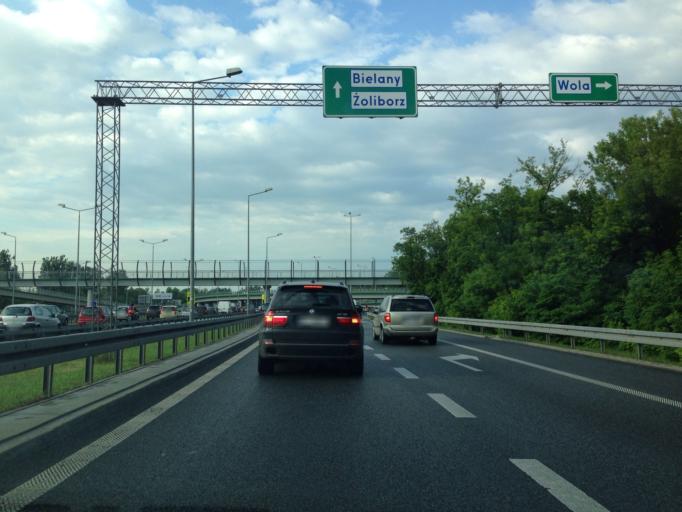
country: PL
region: Masovian Voivodeship
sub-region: Warszawa
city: Bemowo
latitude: 52.2548
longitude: 20.9464
